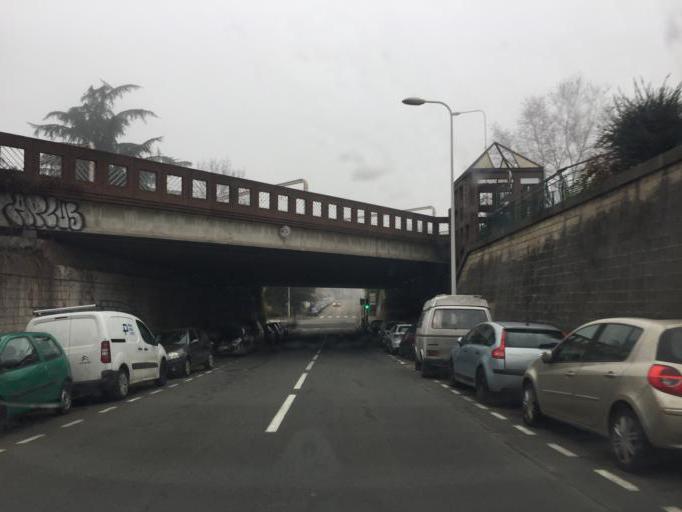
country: FR
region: Rhone-Alpes
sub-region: Departement du Rhone
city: Caluire-et-Cuire
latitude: 45.7822
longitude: 4.8292
